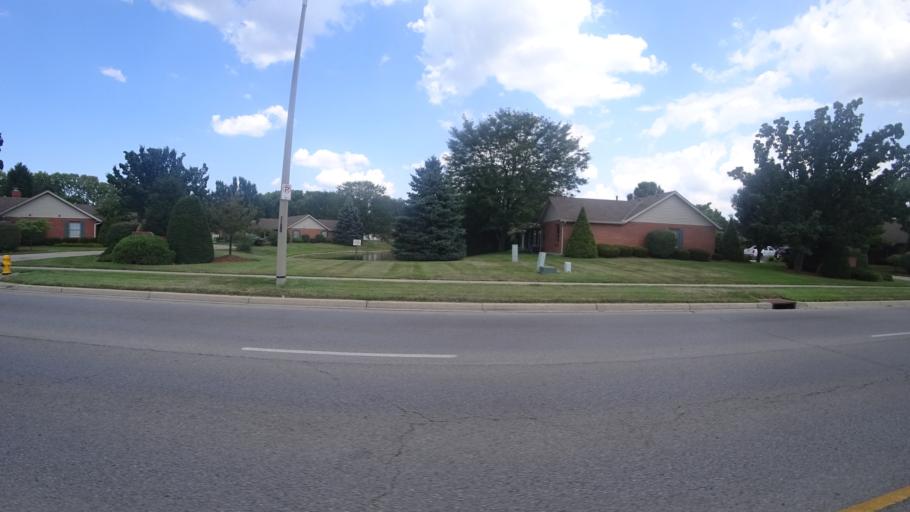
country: US
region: Ohio
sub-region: Butler County
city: Hamilton
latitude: 39.4258
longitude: -84.5865
